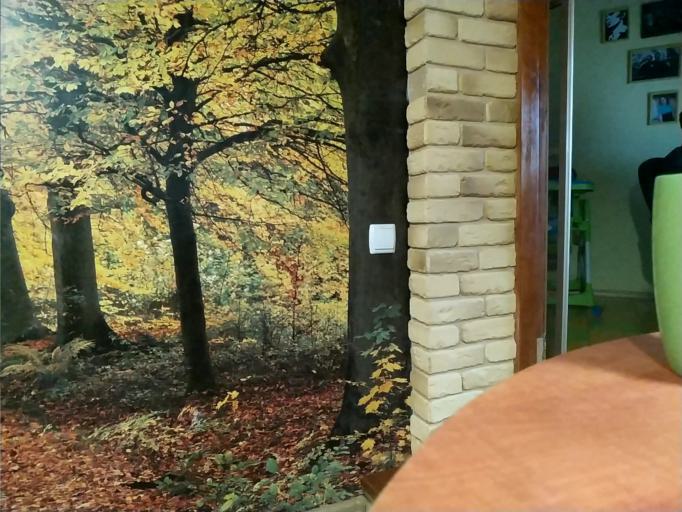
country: RU
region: Tverskaya
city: Staraya Toropa
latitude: 56.3433
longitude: 31.8420
